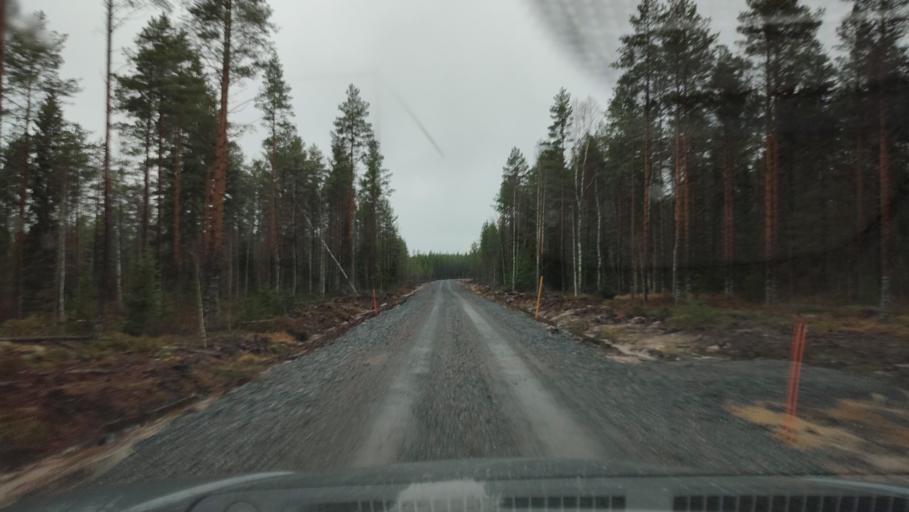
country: FI
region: Southern Ostrobothnia
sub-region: Suupohja
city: Karijoki
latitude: 62.1453
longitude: 21.6134
